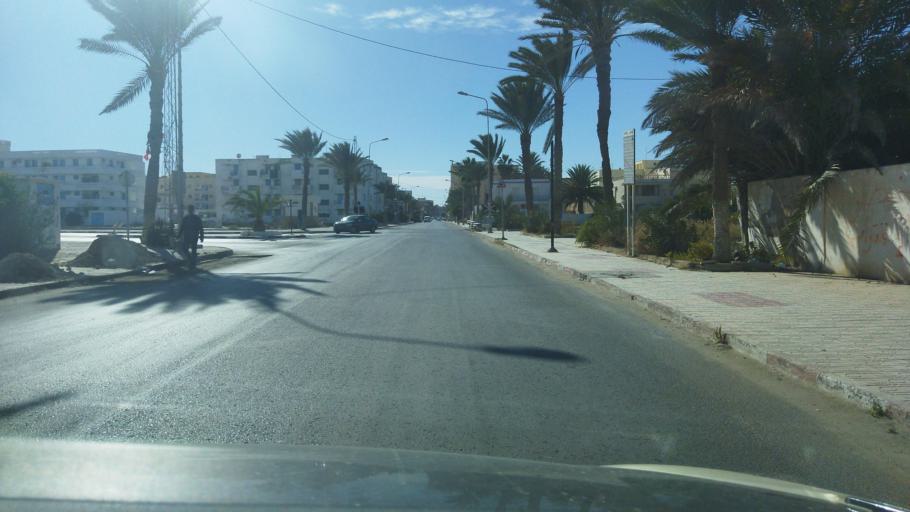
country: TN
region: Qabis
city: Gabes
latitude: 33.8913
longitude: 10.1138
